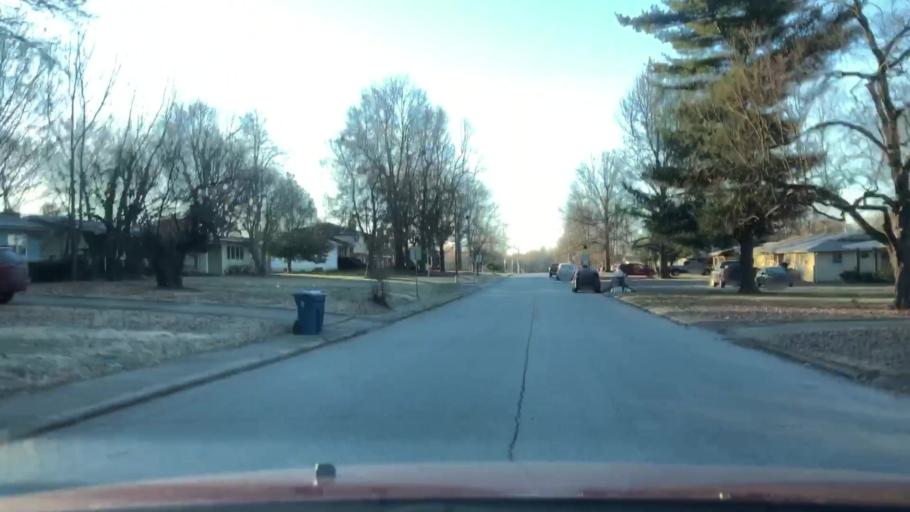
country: US
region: Missouri
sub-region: Greene County
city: Springfield
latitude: 37.1769
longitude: -93.2434
